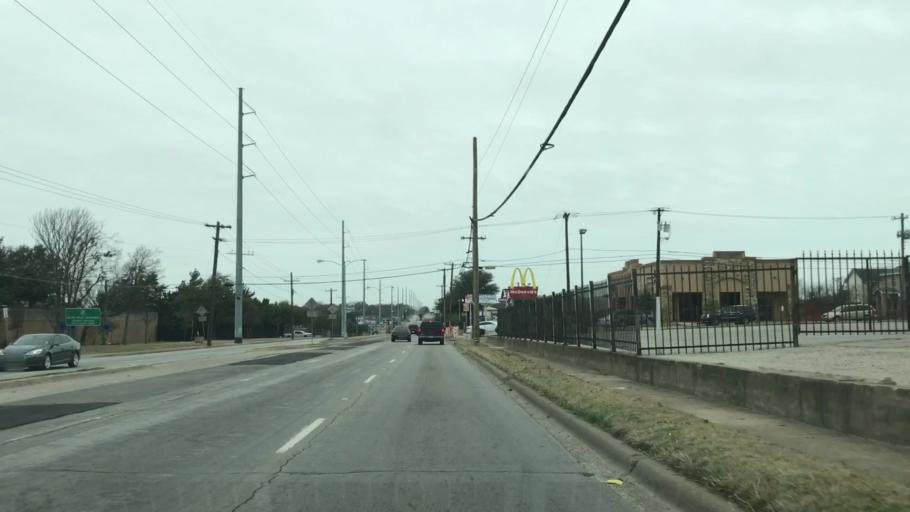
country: US
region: Texas
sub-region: Dallas County
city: Cockrell Hill
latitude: 32.7205
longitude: -96.8875
